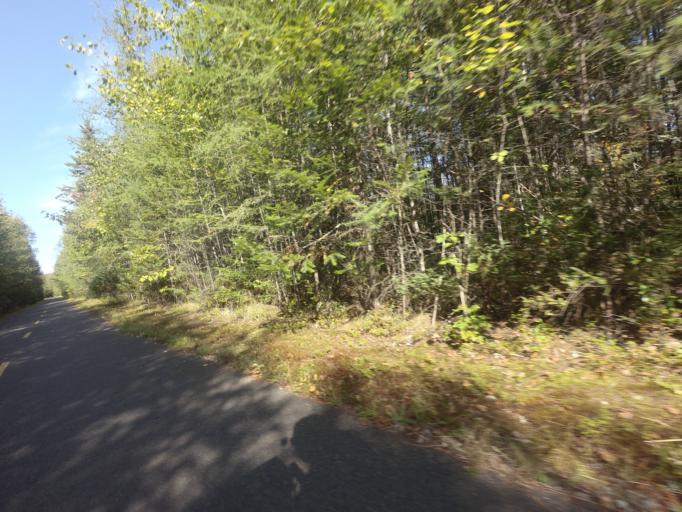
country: CA
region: Quebec
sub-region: Laurentides
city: Mont-Tremblant
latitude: 46.1182
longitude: -74.5183
